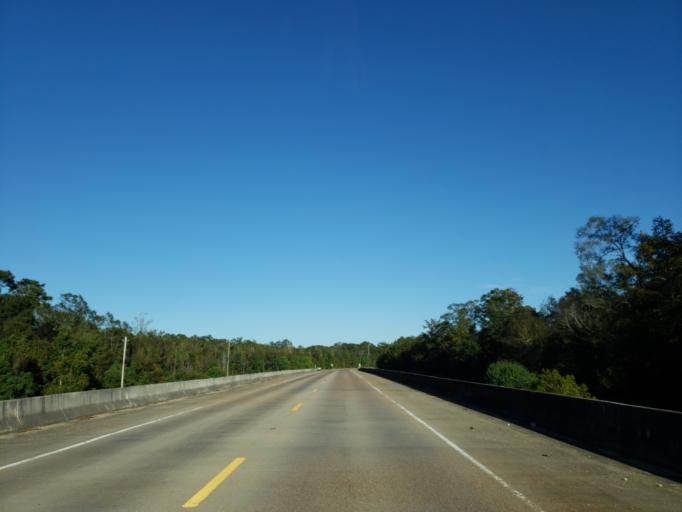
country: US
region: Mississippi
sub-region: Perry County
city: Richton
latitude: 31.3560
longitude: -88.9240
